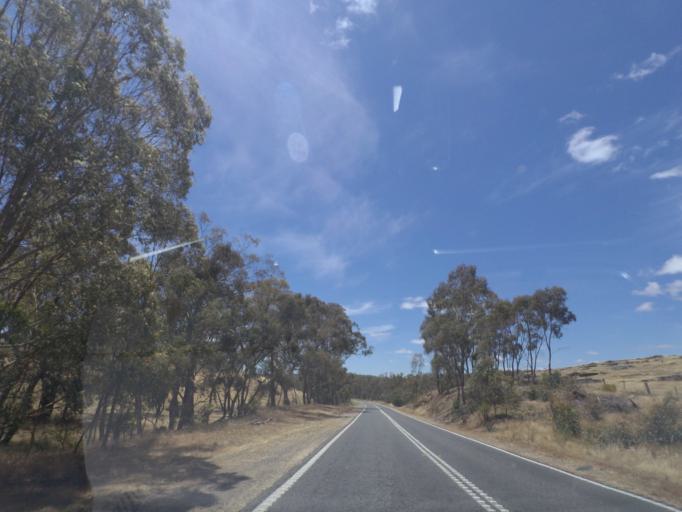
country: AU
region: Victoria
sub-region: Mount Alexander
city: Castlemaine
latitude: -37.2019
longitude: 144.1435
